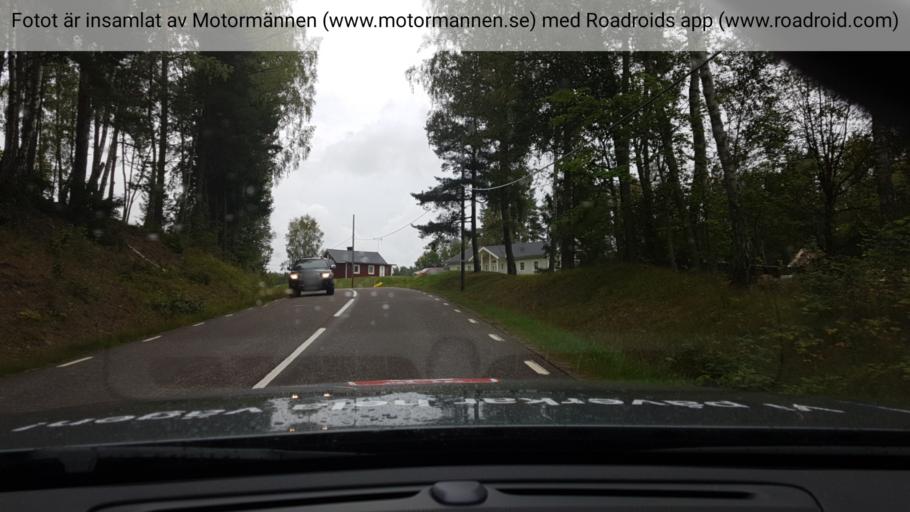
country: SE
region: Stockholm
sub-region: Botkyrka Kommun
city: Varsta
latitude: 59.1129
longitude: 17.8616
